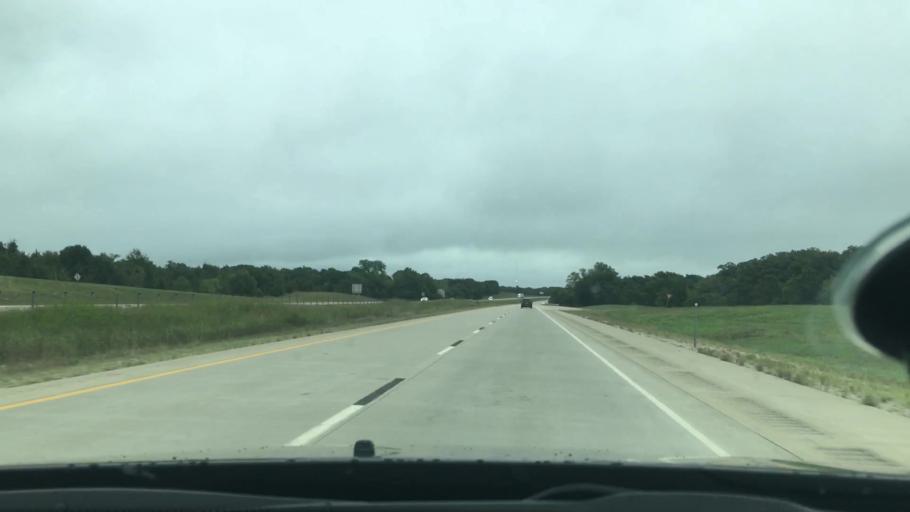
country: US
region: Oklahoma
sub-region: Okfuskee County
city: Boley
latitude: 35.3861
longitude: -96.4582
